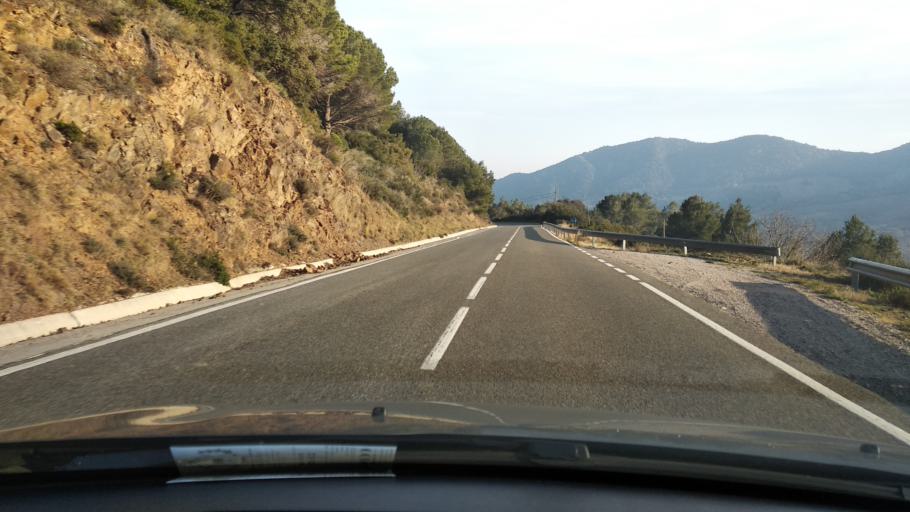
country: ES
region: Catalonia
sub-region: Provincia de Tarragona
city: Alforja
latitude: 41.2186
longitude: 0.9535
